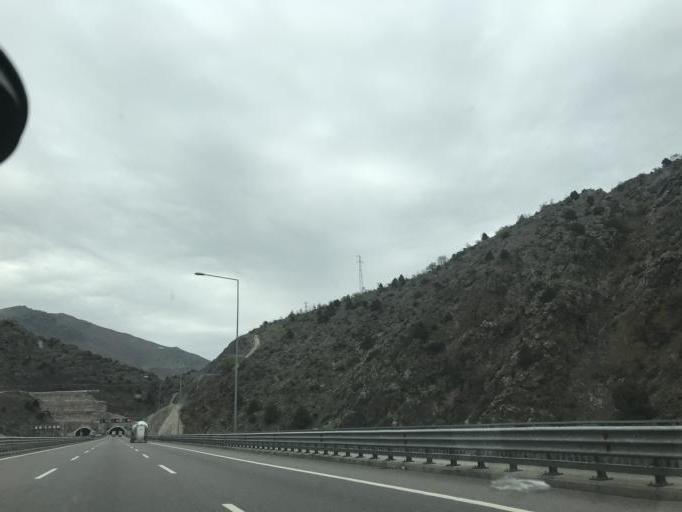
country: TR
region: Nigde
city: Ciftehan
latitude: 37.5548
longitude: 34.7710
